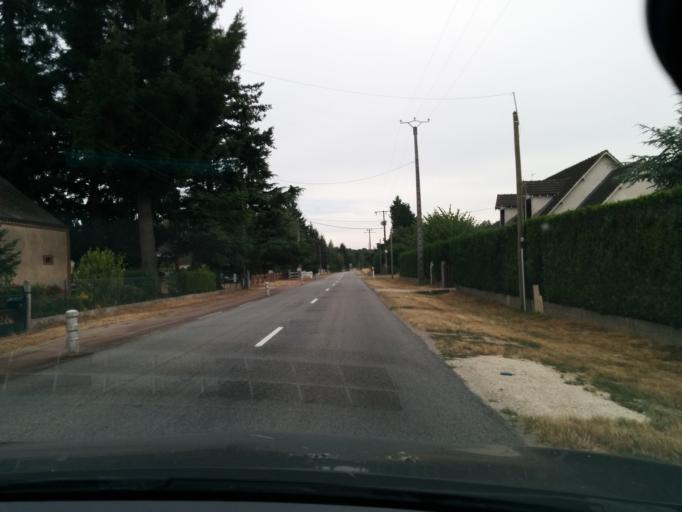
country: FR
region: Centre
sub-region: Departement du Loiret
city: Tigy
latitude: 47.7902
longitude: 2.1986
